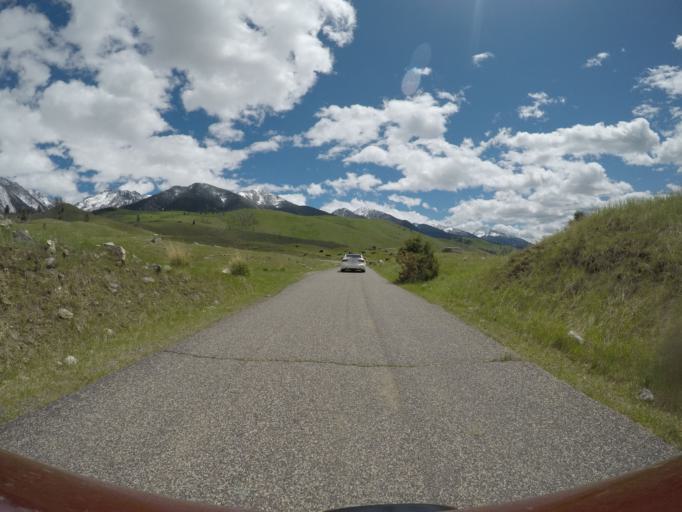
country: US
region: Montana
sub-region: Park County
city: Livingston
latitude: 45.4988
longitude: -110.5559
